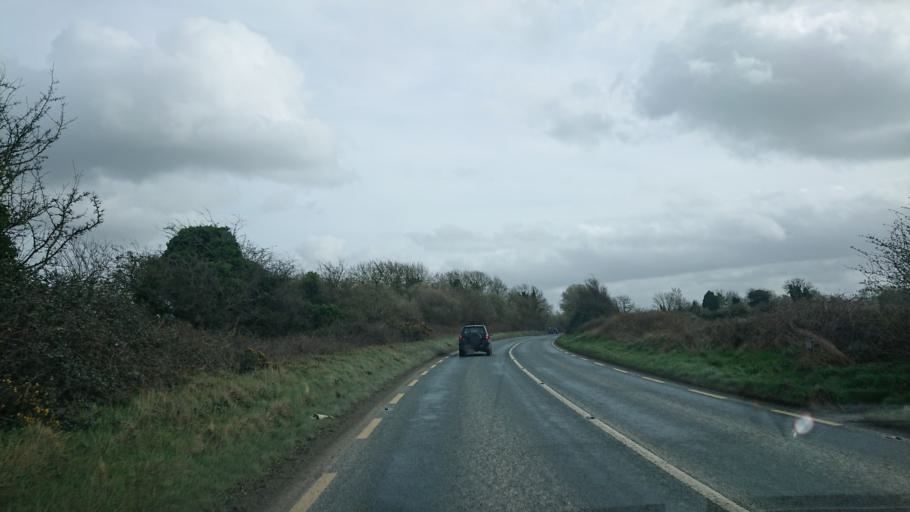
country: IE
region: Leinster
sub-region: Kildare
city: Johnstown
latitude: 53.2046
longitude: -6.6270
